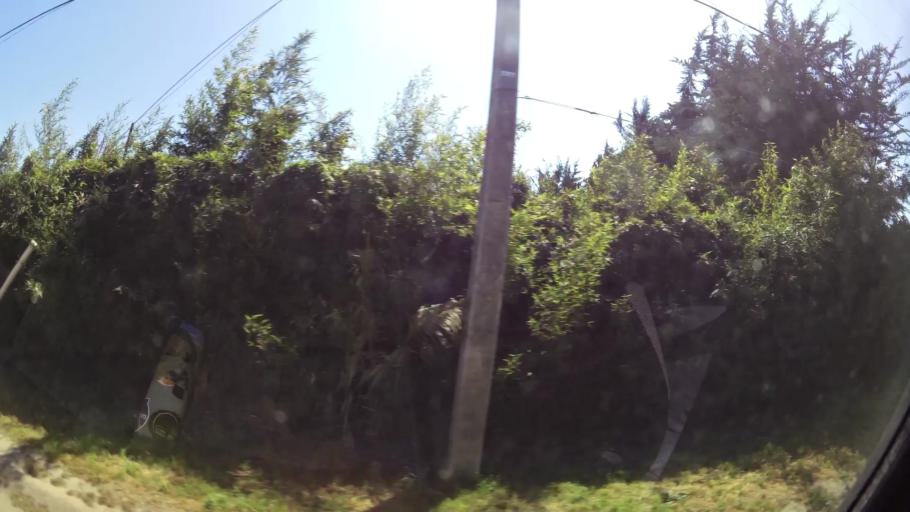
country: CL
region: Santiago Metropolitan
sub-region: Provincia de Talagante
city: Talagante
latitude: -33.6501
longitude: -70.9034
